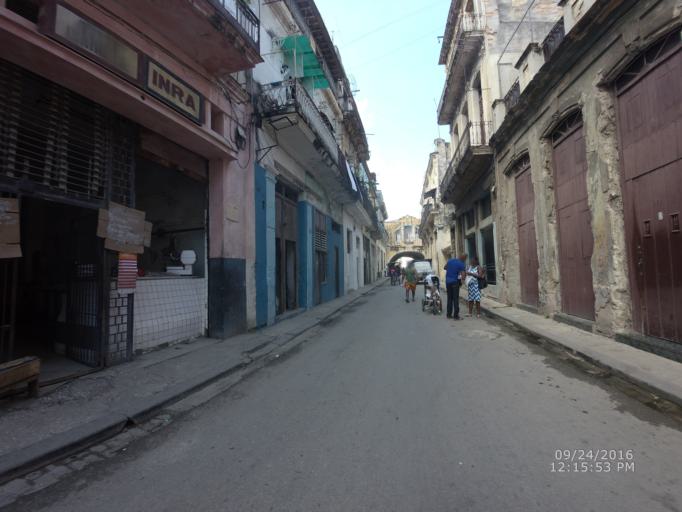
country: CU
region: La Habana
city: La Habana Vieja
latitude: 23.1324
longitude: -82.3518
